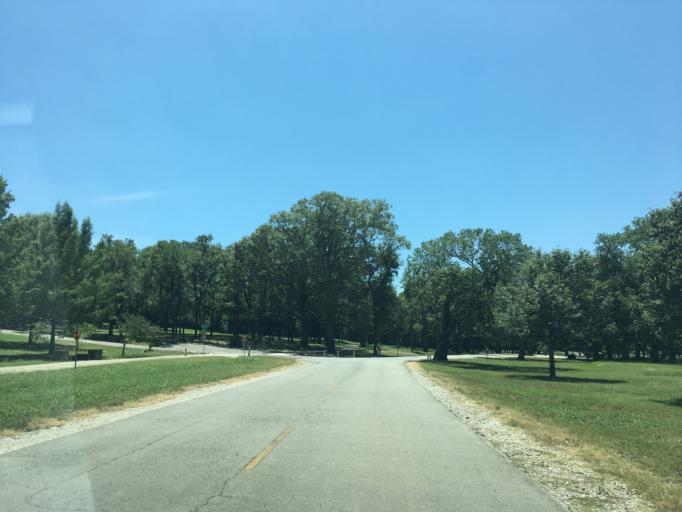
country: US
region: Texas
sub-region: Dallas County
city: Highland Park
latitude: 32.8359
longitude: -96.7075
